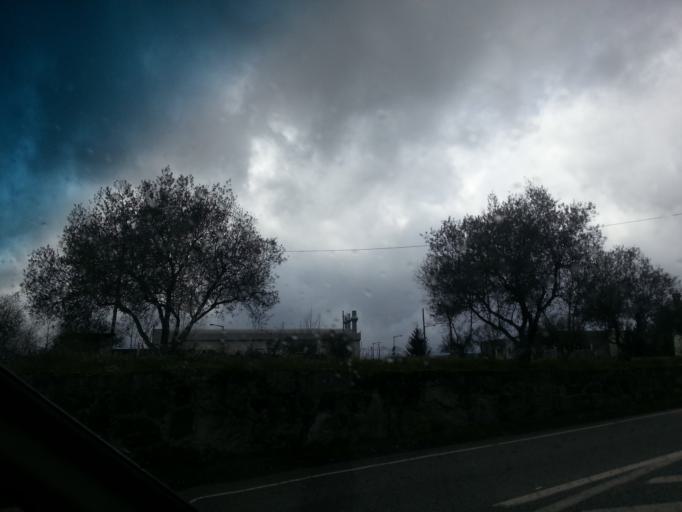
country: PT
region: Viseu
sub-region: Viseu
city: Rio de Loba
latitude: 40.6296
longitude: -7.8642
